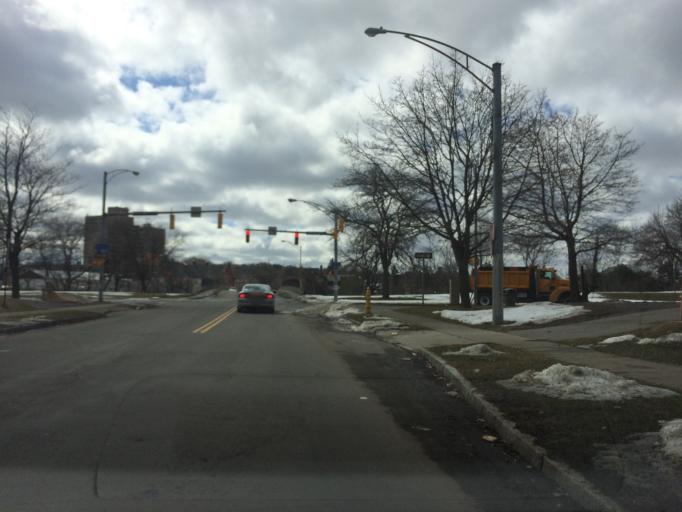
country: US
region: New York
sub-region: Monroe County
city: Rochester
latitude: 43.1438
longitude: -77.5967
